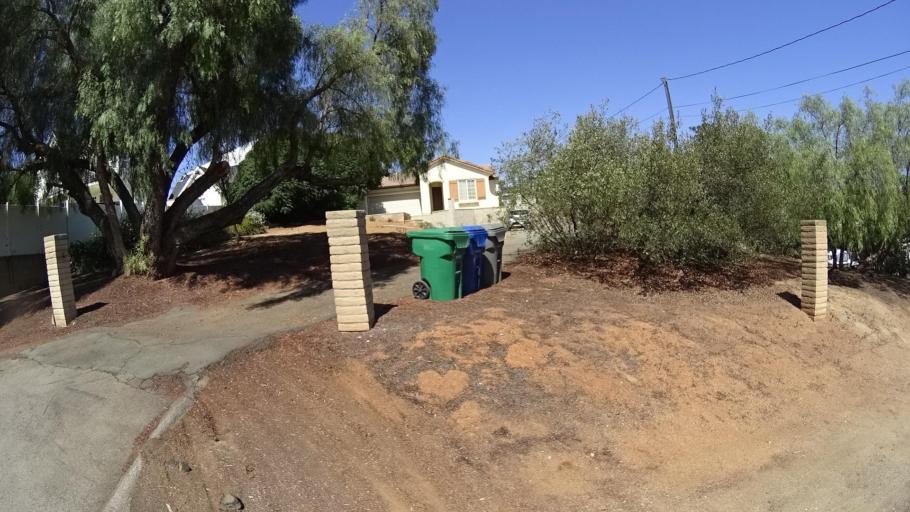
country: US
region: California
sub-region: San Diego County
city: Crest
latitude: 32.8119
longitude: -116.8627
